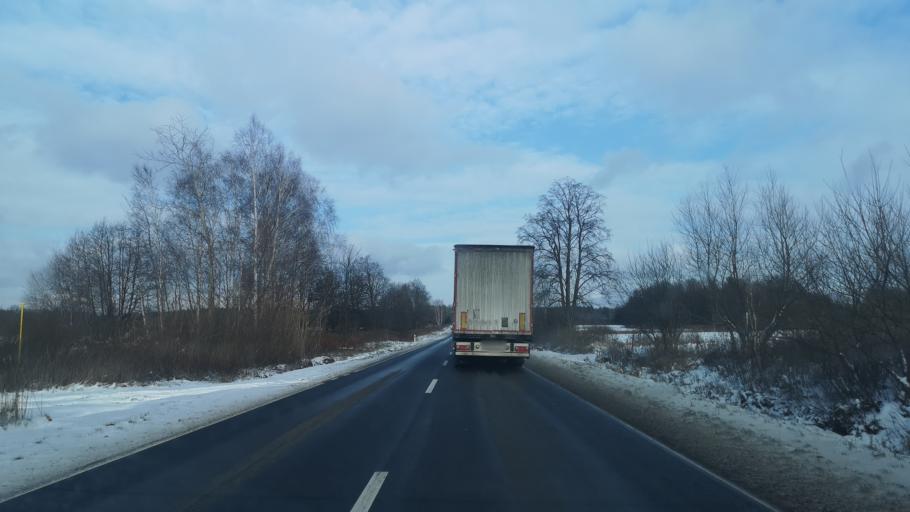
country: PL
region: Subcarpathian Voivodeship
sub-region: Powiat przeworski
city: Sieniawa
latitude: 50.1994
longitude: 22.6309
